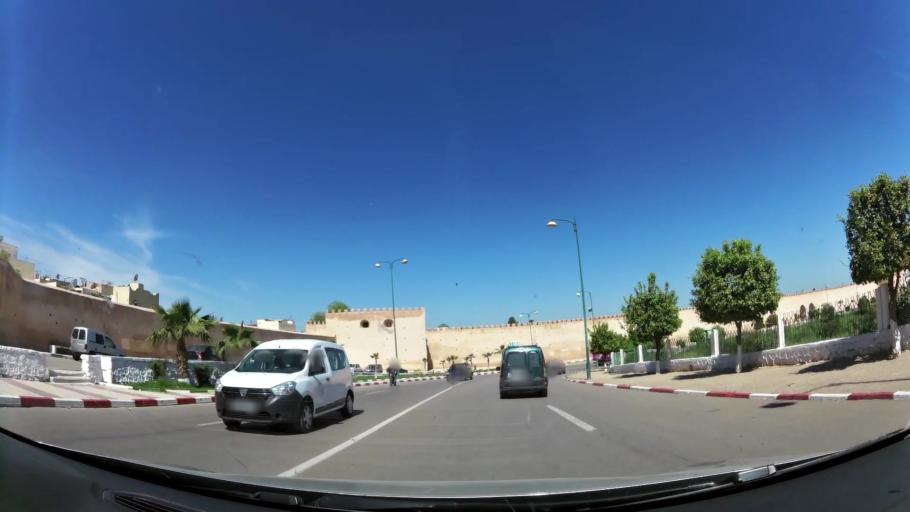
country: MA
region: Meknes-Tafilalet
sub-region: Meknes
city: Meknes
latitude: 33.8851
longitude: -5.5524
